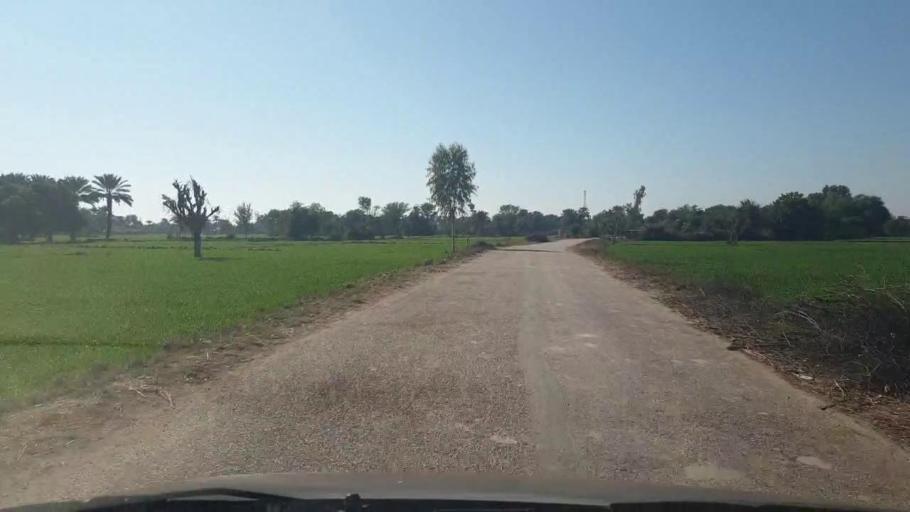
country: PK
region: Sindh
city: Bozdar
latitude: 27.1514
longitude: 68.6533
